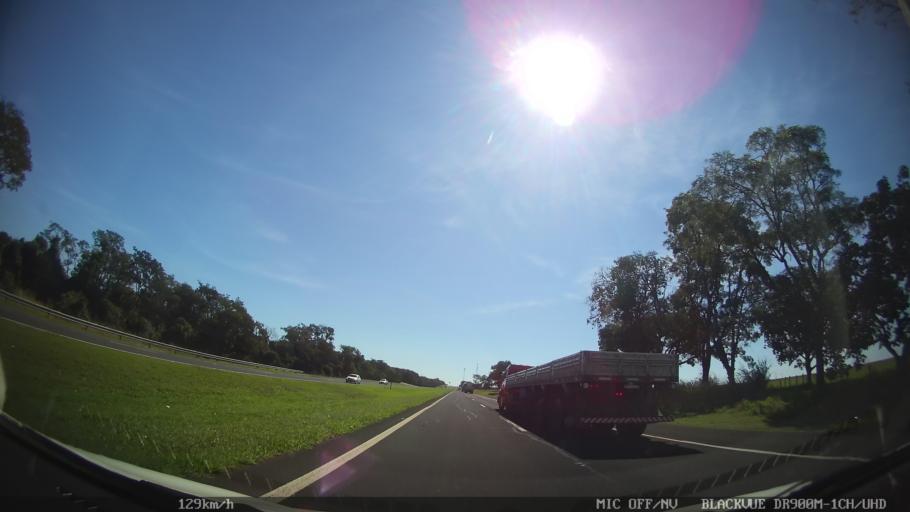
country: BR
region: Sao Paulo
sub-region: Santa Rita Do Passa Quatro
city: Santa Rita do Passa Quatro
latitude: -21.6313
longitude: -47.6134
